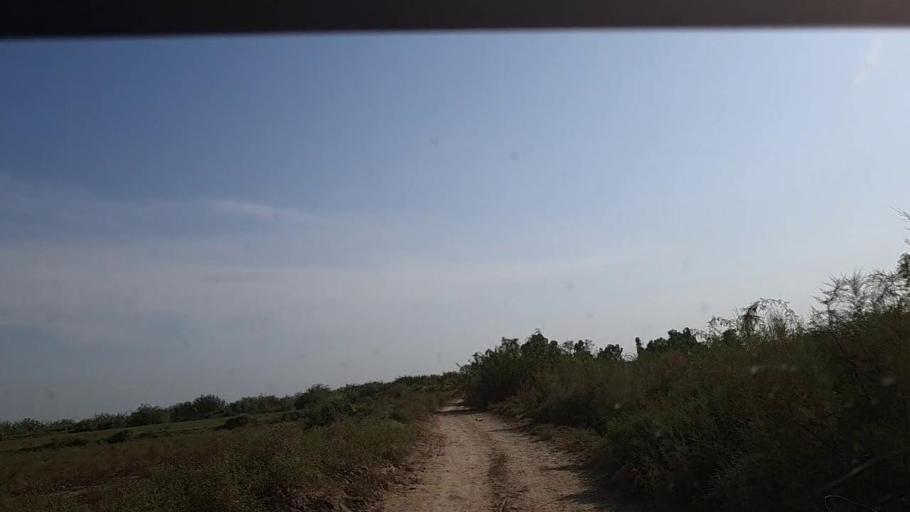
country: PK
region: Sindh
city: Adilpur
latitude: 27.9043
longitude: 69.2334
